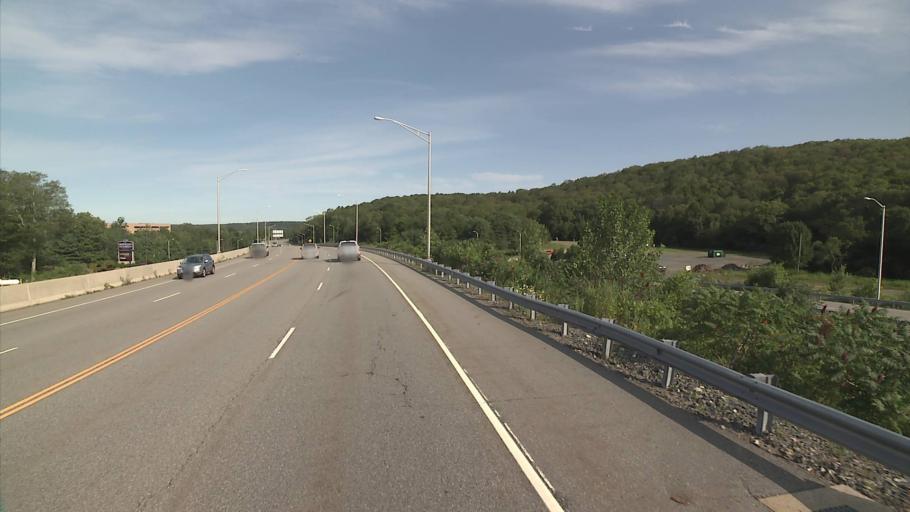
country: US
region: Connecticut
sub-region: New London County
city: Preston City
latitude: 41.4775
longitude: -71.9580
